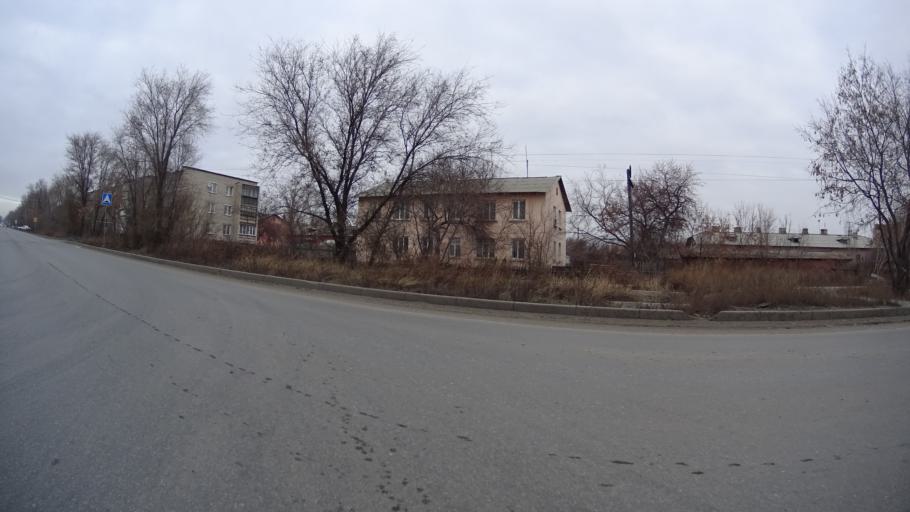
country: RU
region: Chelyabinsk
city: Troitsk
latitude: 54.1081
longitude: 61.5719
